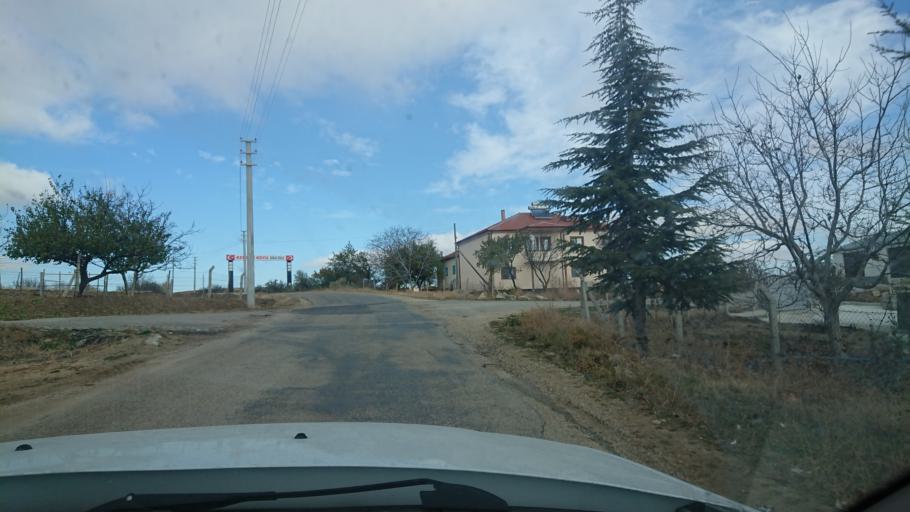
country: TR
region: Aksaray
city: Agacoren
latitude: 38.8266
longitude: 33.9578
